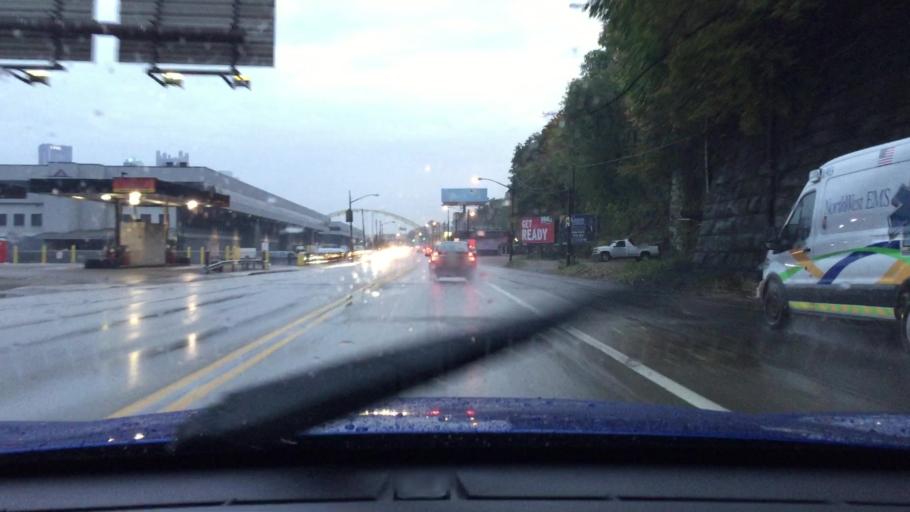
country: US
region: Pennsylvania
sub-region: Allegheny County
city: Pittsburgh
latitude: 40.4431
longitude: -80.0255
